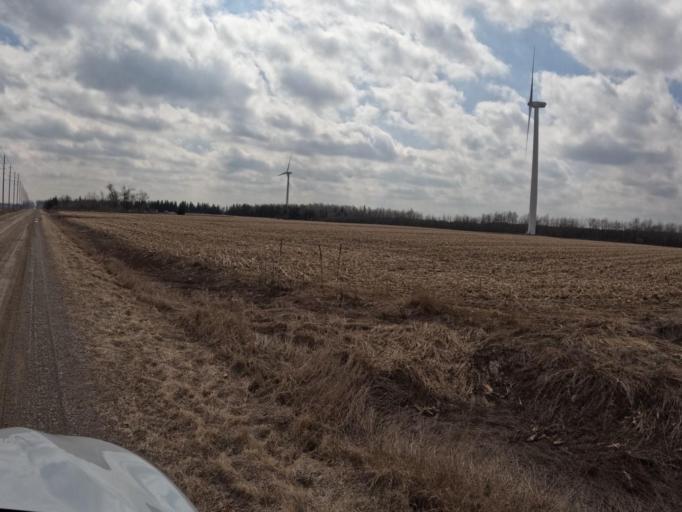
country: CA
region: Ontario
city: Shelburne
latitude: 44.0338
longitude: -80.3160
